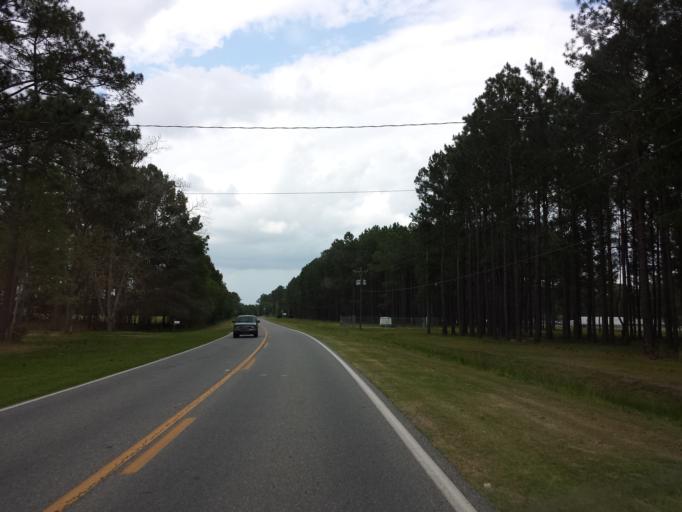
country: US
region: Georgia
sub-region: Cook County
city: Sparks
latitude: 31.2191
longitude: -83.4552
